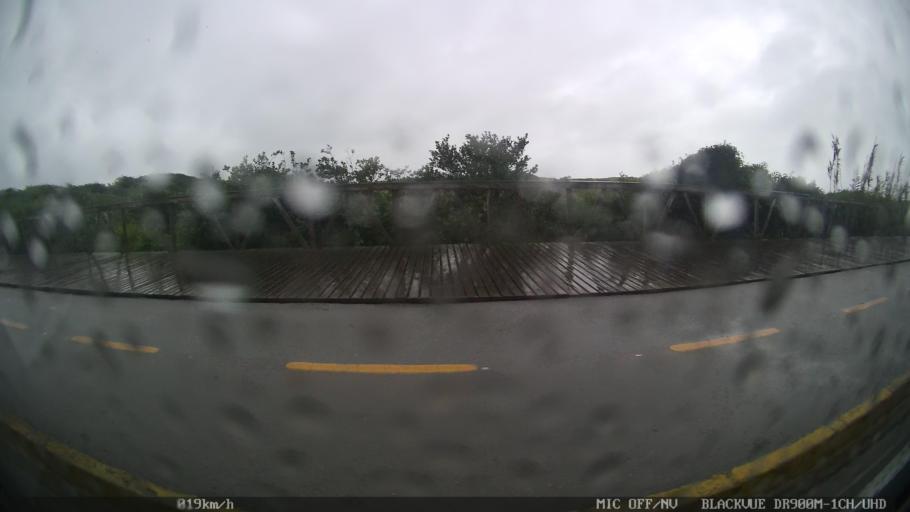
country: BR
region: Santa Catarina
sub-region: Navegantes
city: Navegantes
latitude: -26.8886
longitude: -48.6423
